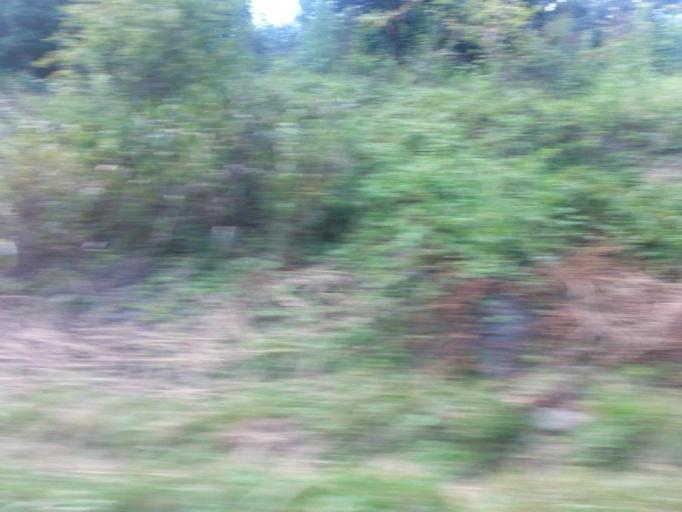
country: US
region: Virginia
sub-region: Washington County
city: Abingdon
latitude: 36.6942
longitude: -81.9739
